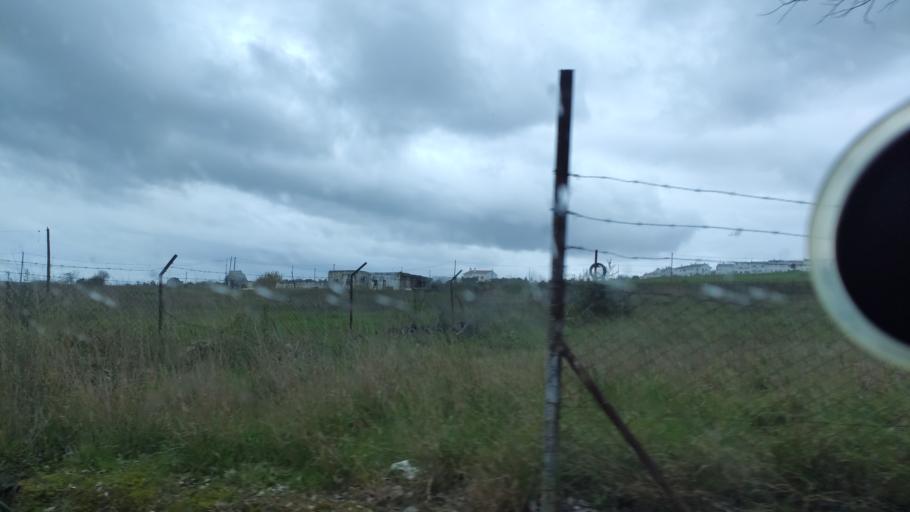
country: PT
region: Beja
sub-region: Beja
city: Beja
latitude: 38.0133
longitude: -7.8499
